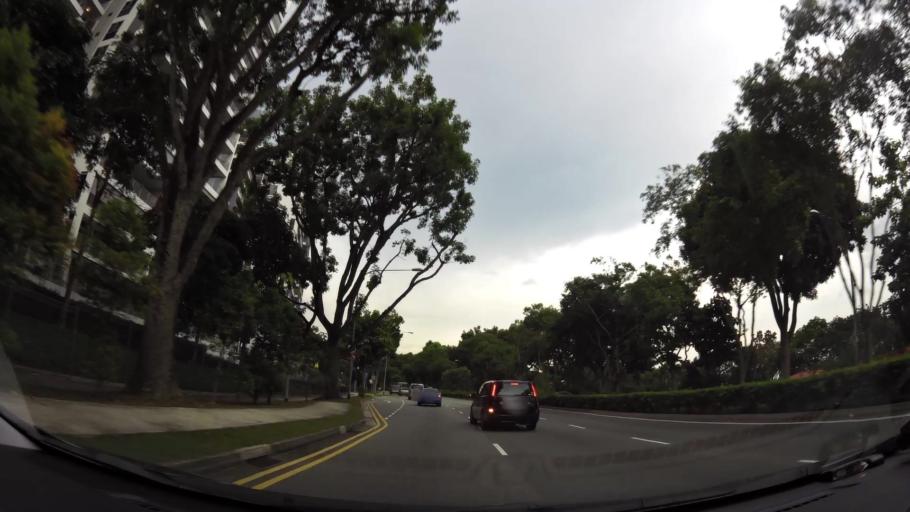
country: MY
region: Johor
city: Kampung Pasir Gudang Baru
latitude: 1.4103
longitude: 103.8317
